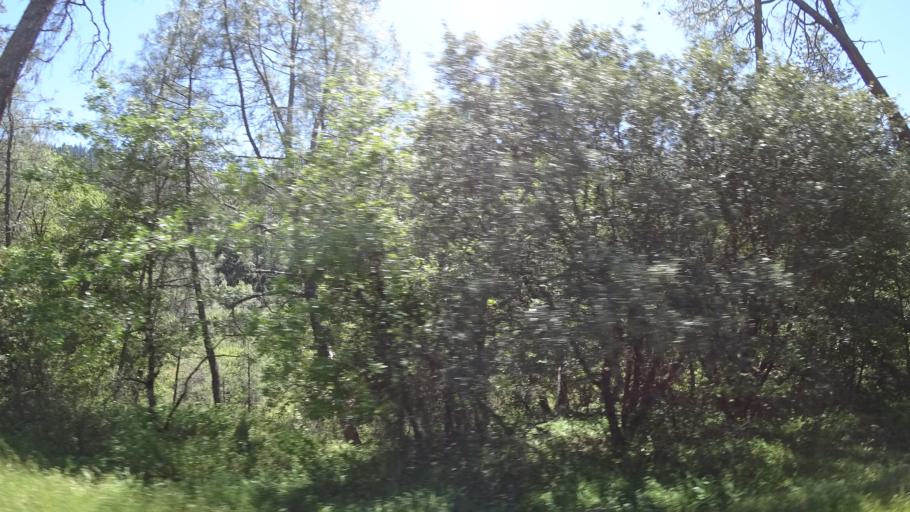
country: US
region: California
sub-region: Trinity County
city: Hayfork
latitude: 40.7410
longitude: -123.2557
